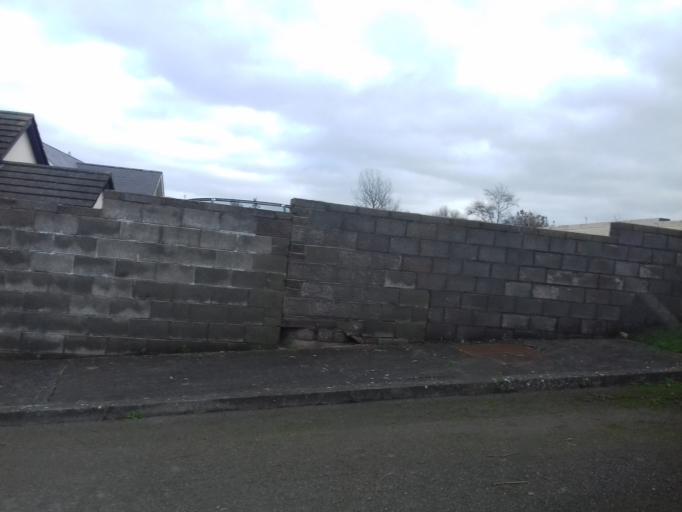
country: IE
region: Leinster
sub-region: An Mhi
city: Duleek
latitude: 53.6912
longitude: -6.4208
